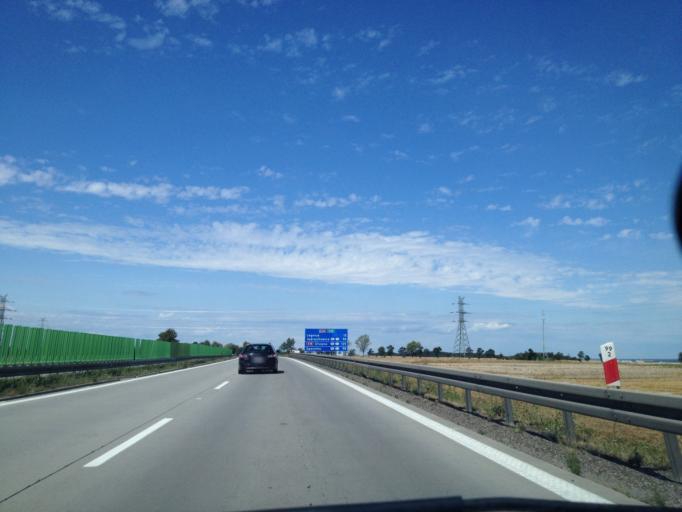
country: PL
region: Lower Silesian Voivodeship
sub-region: Powiat legnicki
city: Legnickie Pole
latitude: 51.1462
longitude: 16.2674
